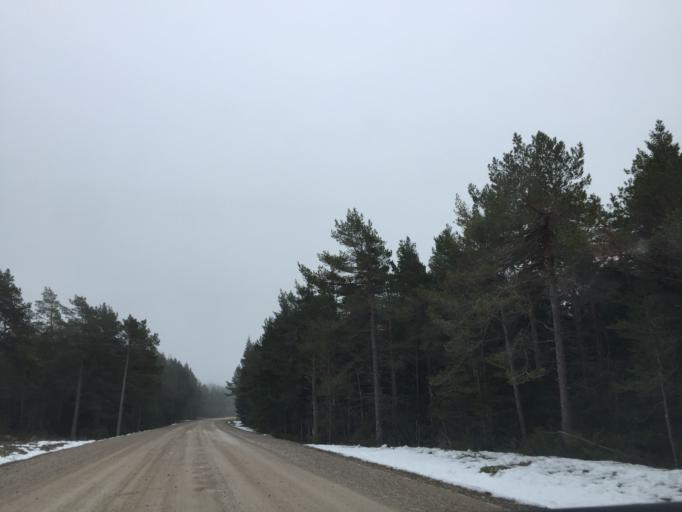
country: EE
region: Saare
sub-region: Kuressaare linn
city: Kuressaare
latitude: 58.4860
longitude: 21.9943
